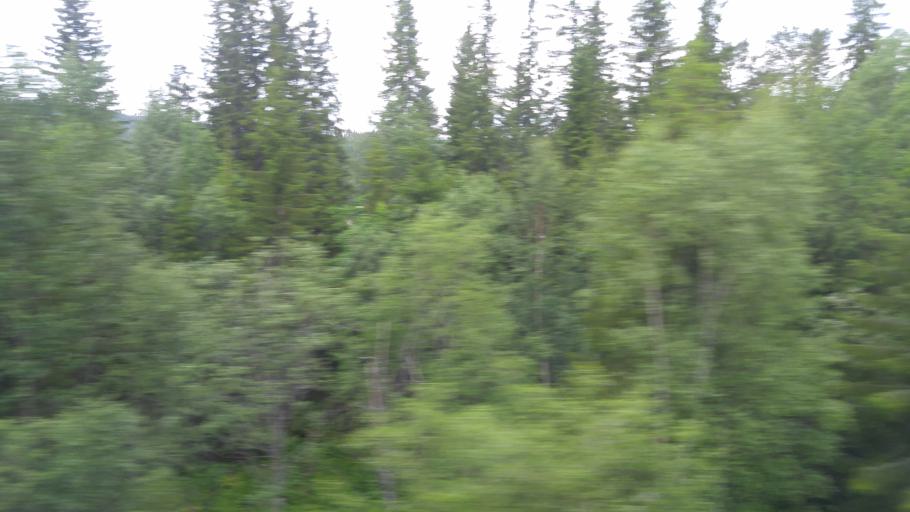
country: NO
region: Nord-Trondelag
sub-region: Meraker
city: Meraker
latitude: 63.3917
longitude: 11.8503
